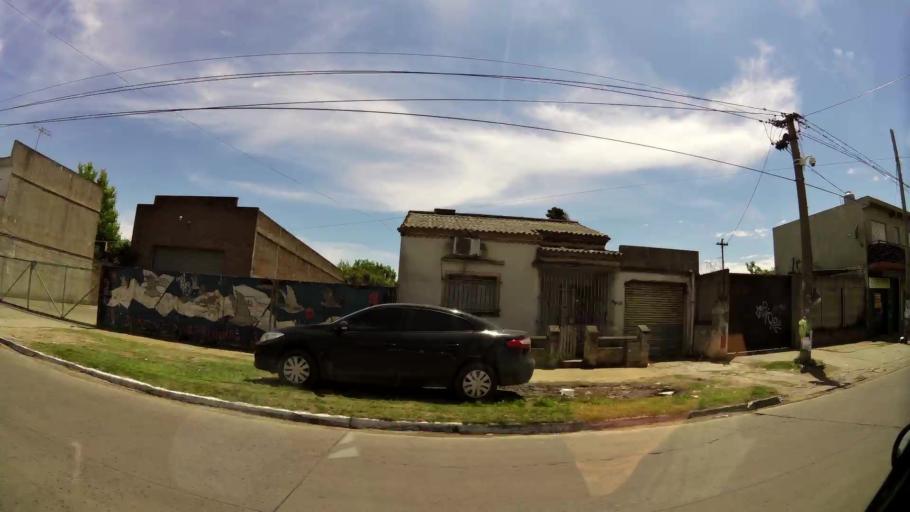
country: AR
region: Buenos Aires
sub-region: Partido de Quilmes
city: Quilmes
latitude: -34.7840
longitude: -58.2685
